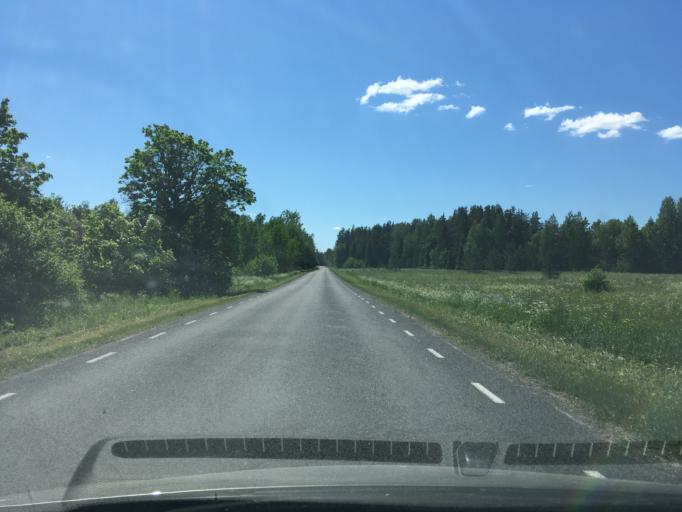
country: EE
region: Raplamaa
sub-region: Kohila vald
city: Kohila
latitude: 59.1517
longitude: 24.8521
